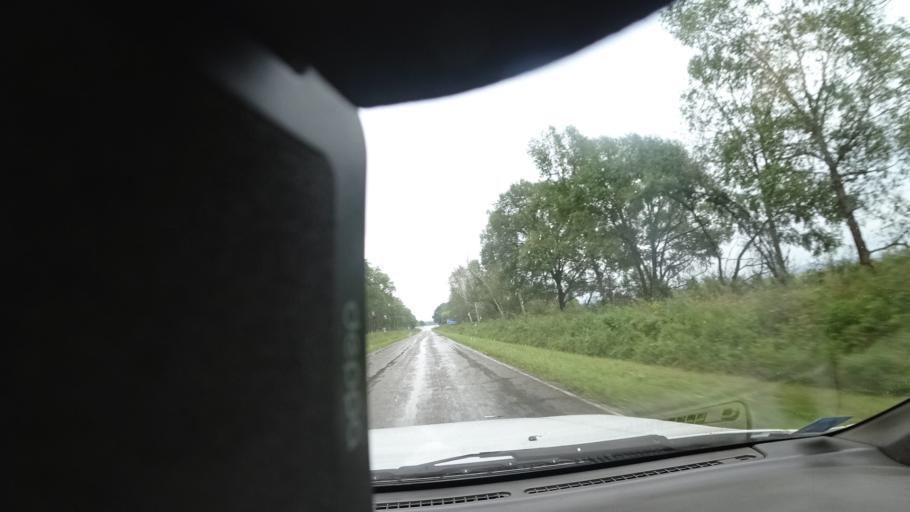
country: RU
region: Primorskiy
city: Dal'nerechensk
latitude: 45.8701
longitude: 133.7174
